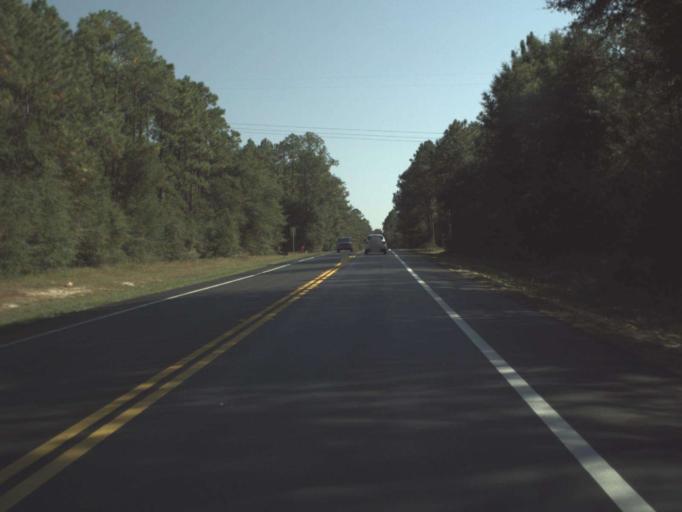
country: US
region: Florida
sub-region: Walton County
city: DeFuniak Springs
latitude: 30.7583
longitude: -86.1514
